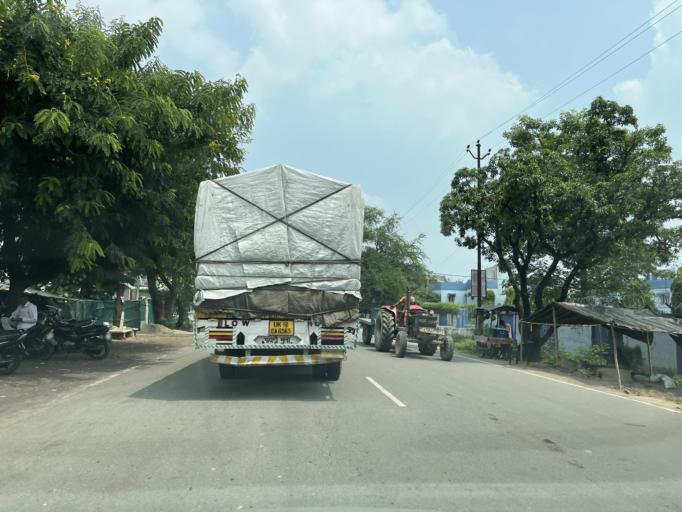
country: IN
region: Uttar Pradesh
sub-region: Bijnor
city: Najibabad
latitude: 29.6009
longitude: 78.3409
